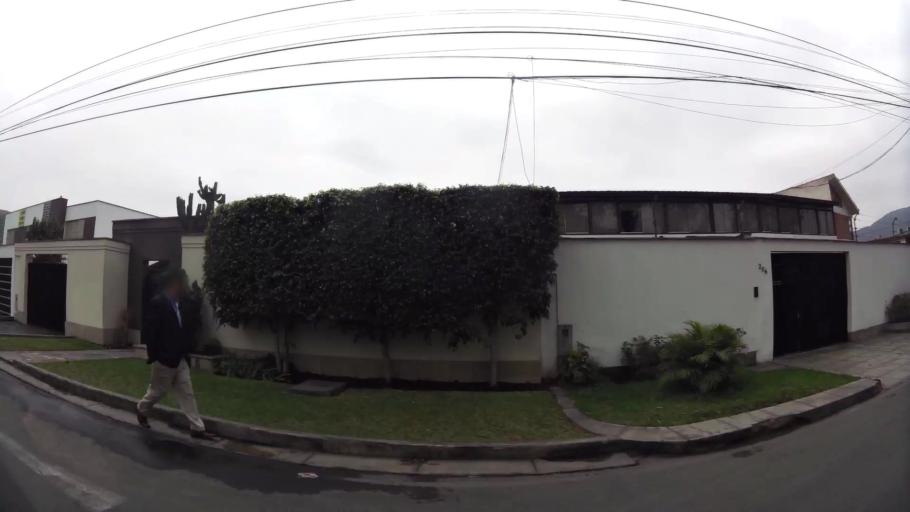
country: PE
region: Lima
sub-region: Lima
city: La Molina
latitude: -12.0862
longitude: -76.9241
